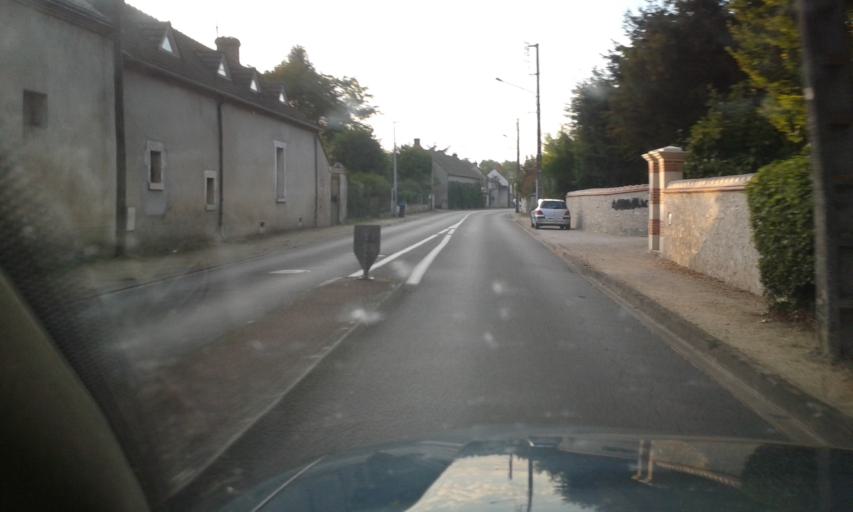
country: FR
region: Centre
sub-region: Departement du Loiret
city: Saint-Pryve-Saint-Mesmin
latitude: 47.8680
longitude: 1.8672
